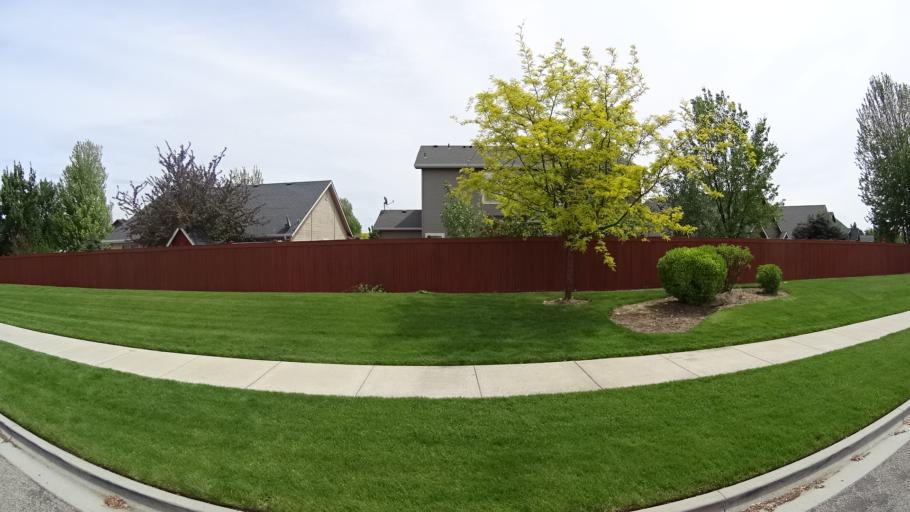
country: US
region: Idaho
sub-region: Ada County
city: Meridian
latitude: 43.5497
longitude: -116.3243
